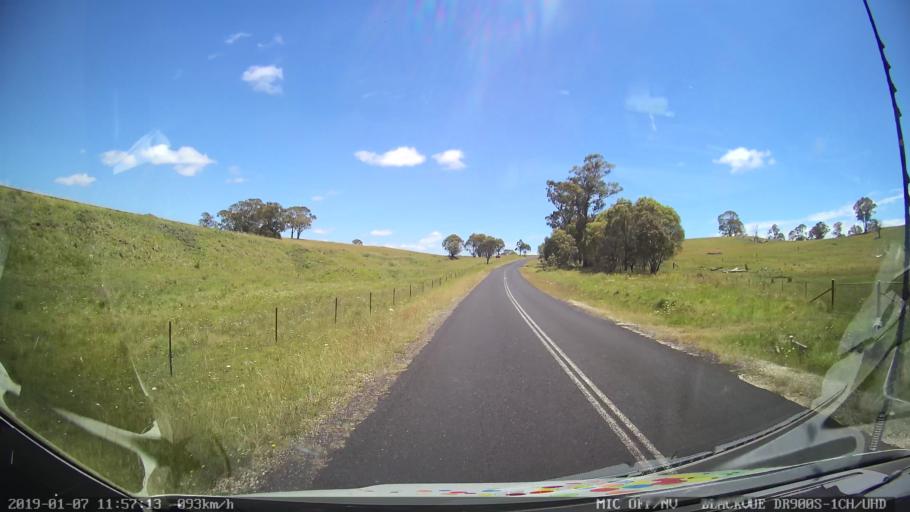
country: AU
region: New South Wales
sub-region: Guyra
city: Guyra
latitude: -30.2671
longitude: 151.6667
